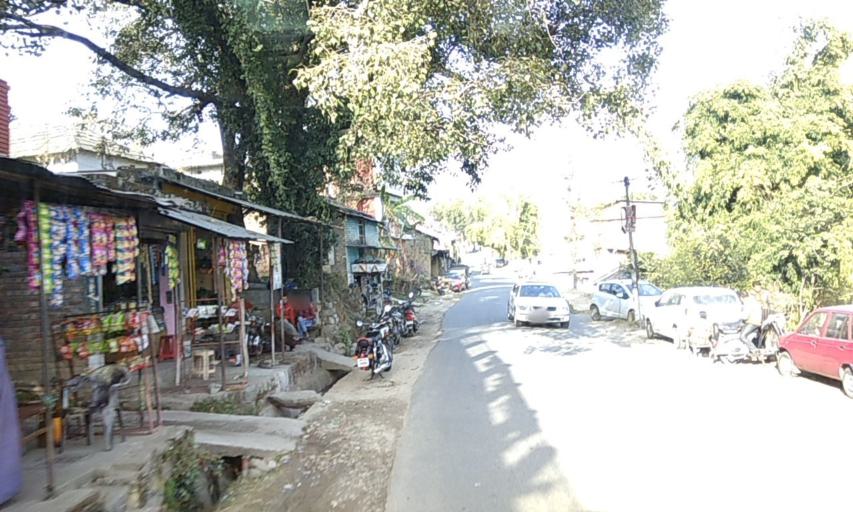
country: IN
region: Himachal Pradesh
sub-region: Kangra
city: Palampur
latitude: 32.0843
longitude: 76.5231
